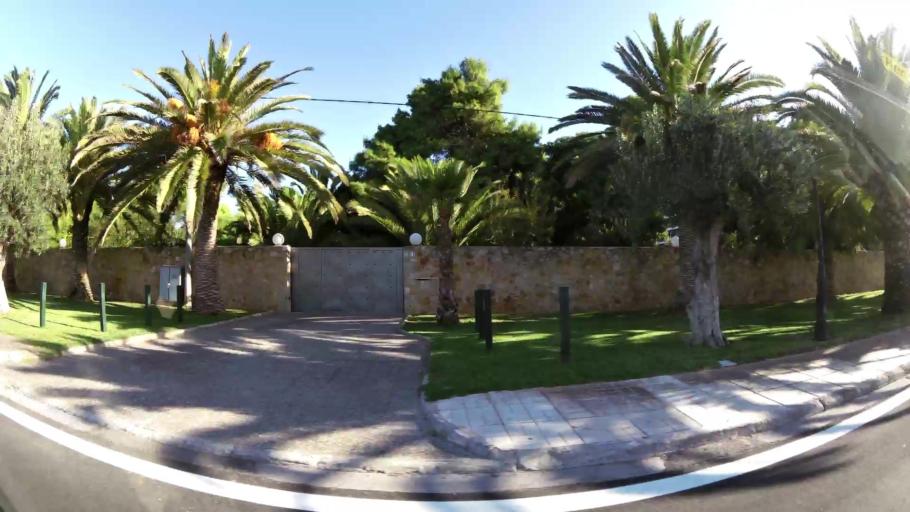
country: GR
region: Attica
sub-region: Nomarchia Athinas
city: Glyfada
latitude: 37.8656
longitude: 23.7415
